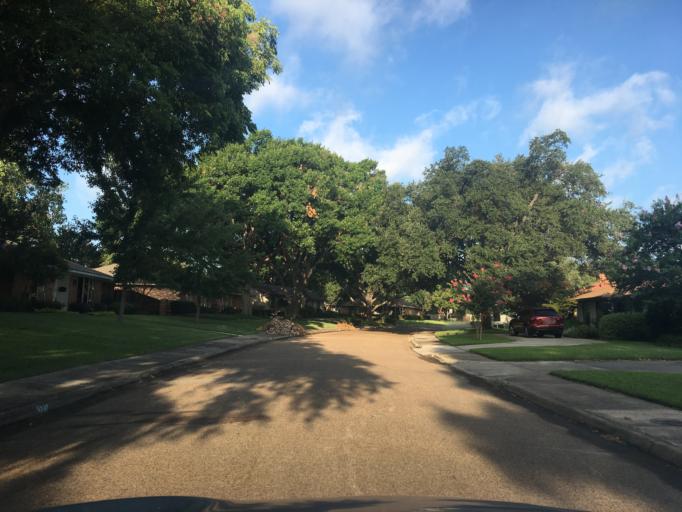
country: US
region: Texas
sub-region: Dallas County
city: Highland Park
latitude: 32.8485
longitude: -96.7594
